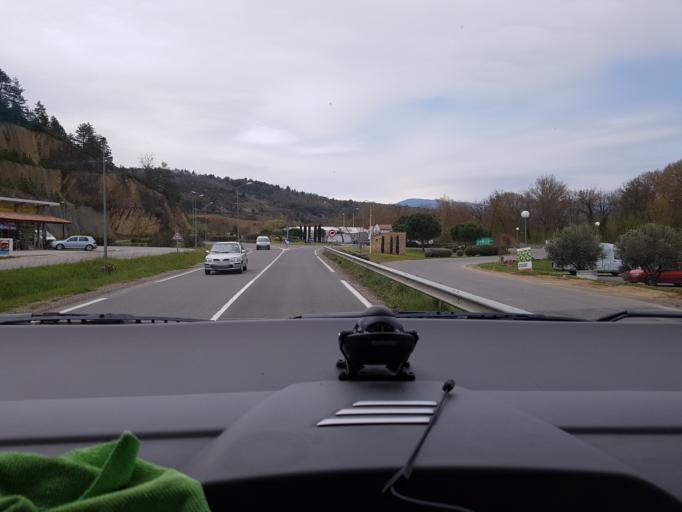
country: FR
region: Languedoc-Roussillon
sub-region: Departement de l'Aude
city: Esperaza
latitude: 42.9374
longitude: 2.2357
